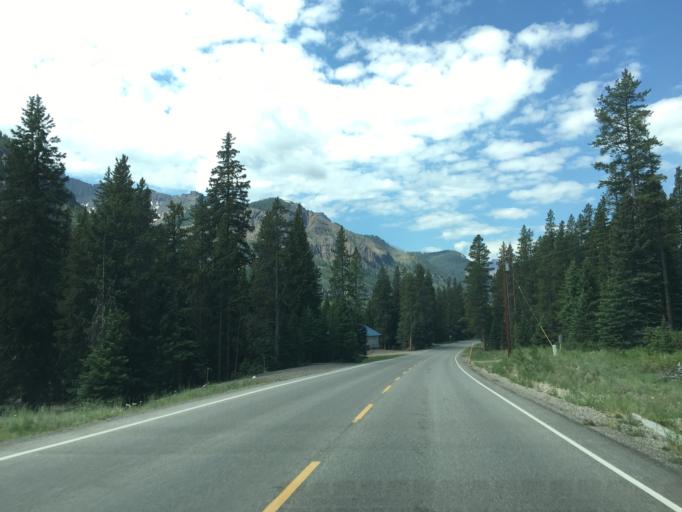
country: US
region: Montana
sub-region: Stillwater County
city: Absarokee
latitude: 45.0098
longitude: -109.9780
